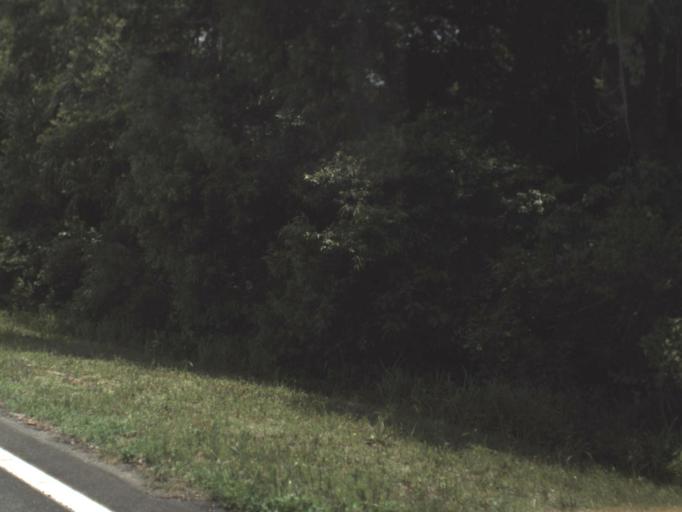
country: US
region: Florida
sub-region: Levy County
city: Chiefland
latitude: 29.2976
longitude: -82.8211
